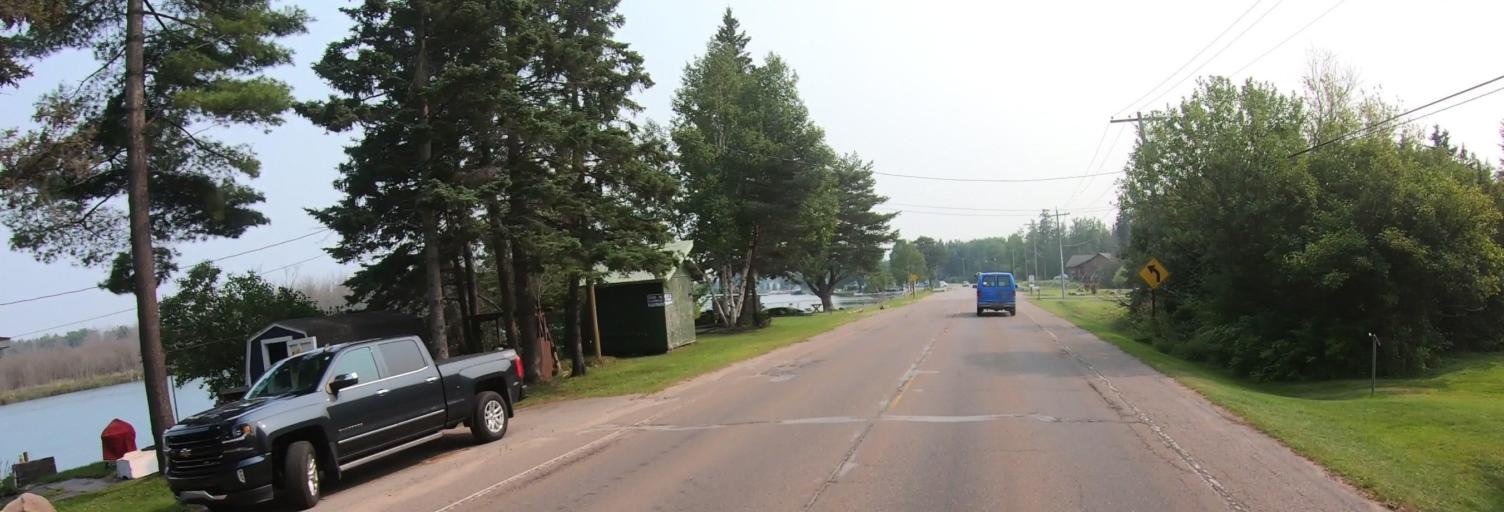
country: US
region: Michigan
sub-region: Chippewa County
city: Sault Ste. Marie
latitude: 46.4793
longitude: -84.3041
